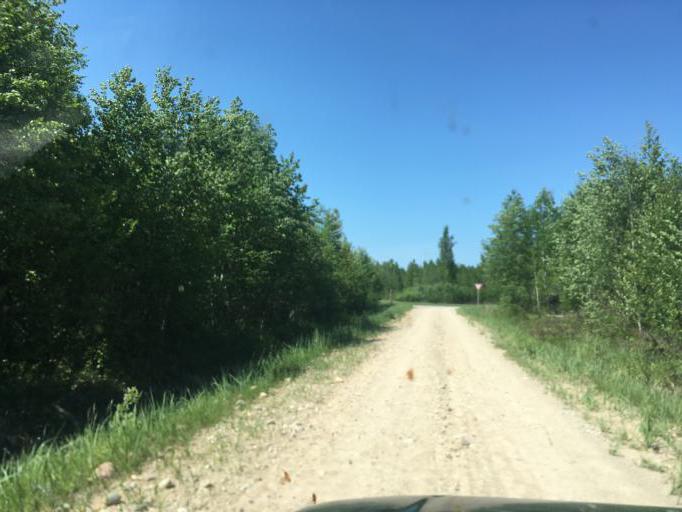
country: LV
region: Talsu Rajons
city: Valdemarpils
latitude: 57.4494
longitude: 22.6555
